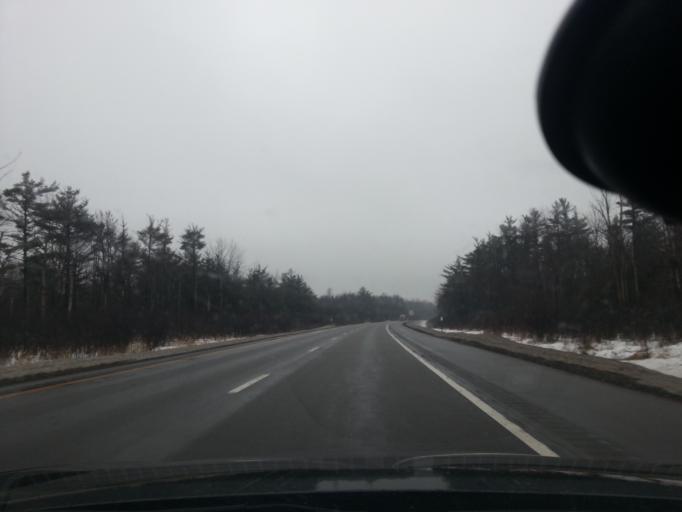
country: US
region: New York
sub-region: Oswego County
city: Pulaski
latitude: 43.6711
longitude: -76.0705
